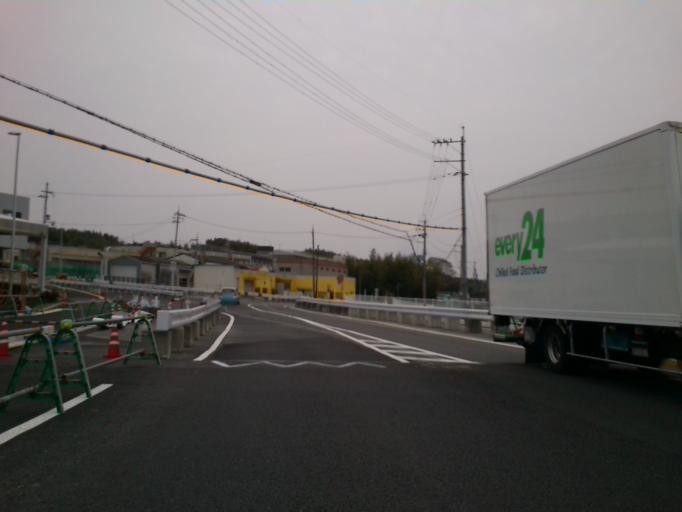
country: JP
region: Kyoto
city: Yawata
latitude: 34.8507
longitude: 135.7241
